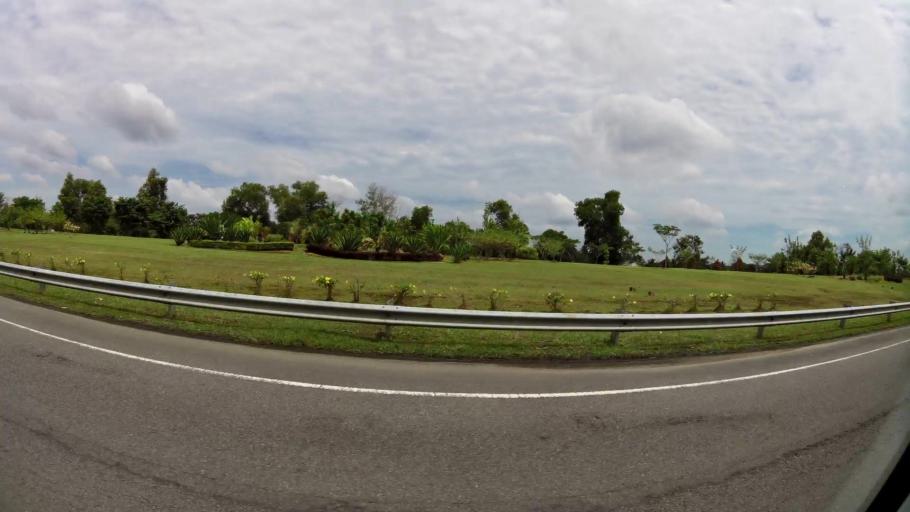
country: BN
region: Brunei and Muara
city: Bandar Seri Begawan
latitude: 4.9340
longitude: 114.9284
